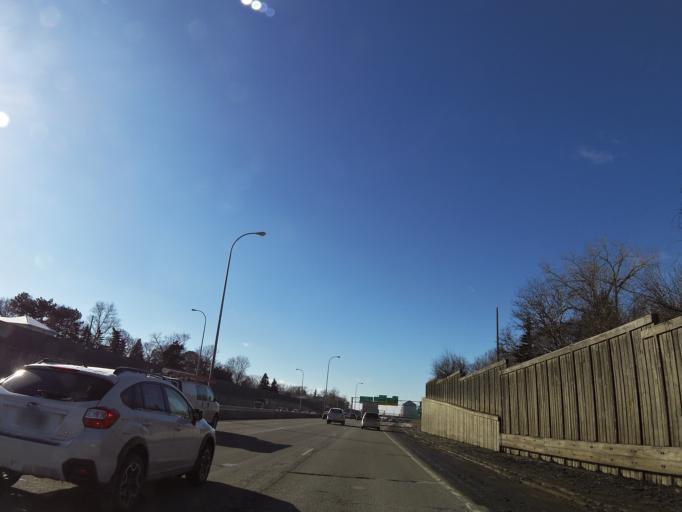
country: US
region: Minnesota
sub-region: Hennepin County
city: Saint Louis Park
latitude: 44.9705
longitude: -93.3278
